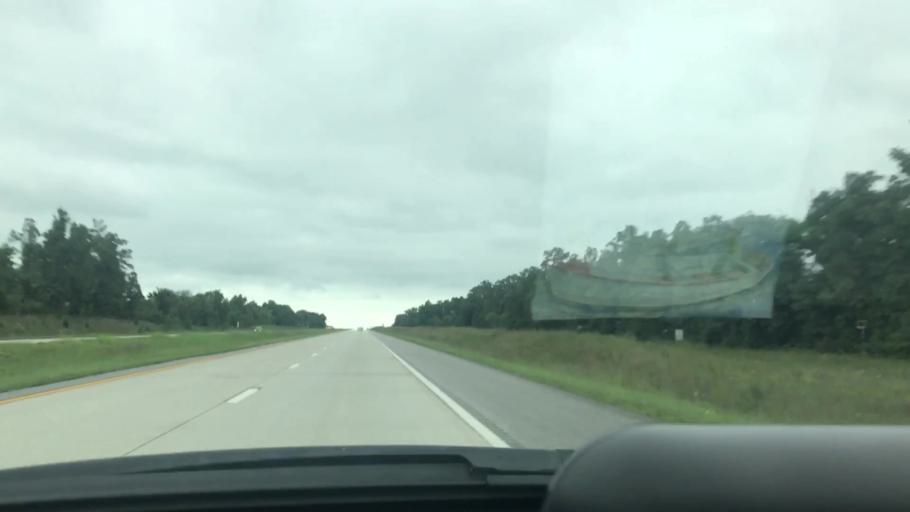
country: US
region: Missouri
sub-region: Greene County
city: Fair Grove
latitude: 37.4750
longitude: -93.1394
